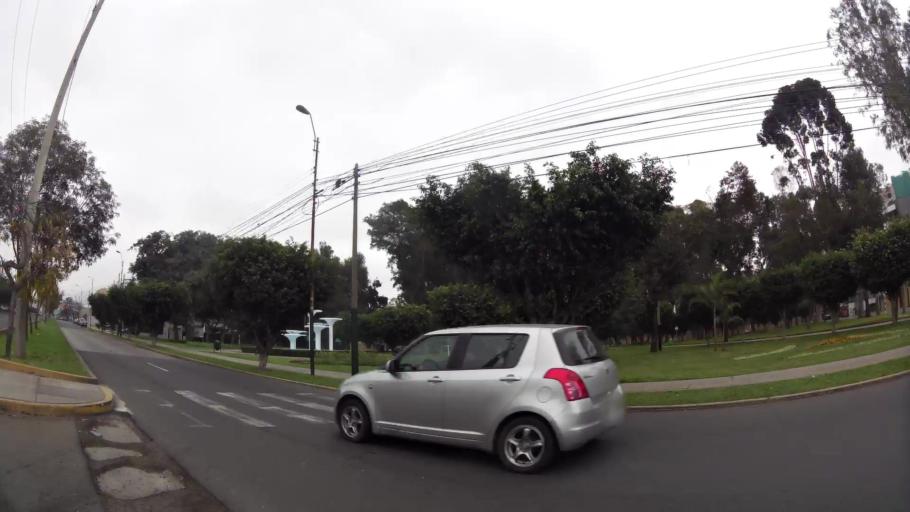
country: PE
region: Lima
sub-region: Lima
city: Surco
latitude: -12.1111
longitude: -76.9883
